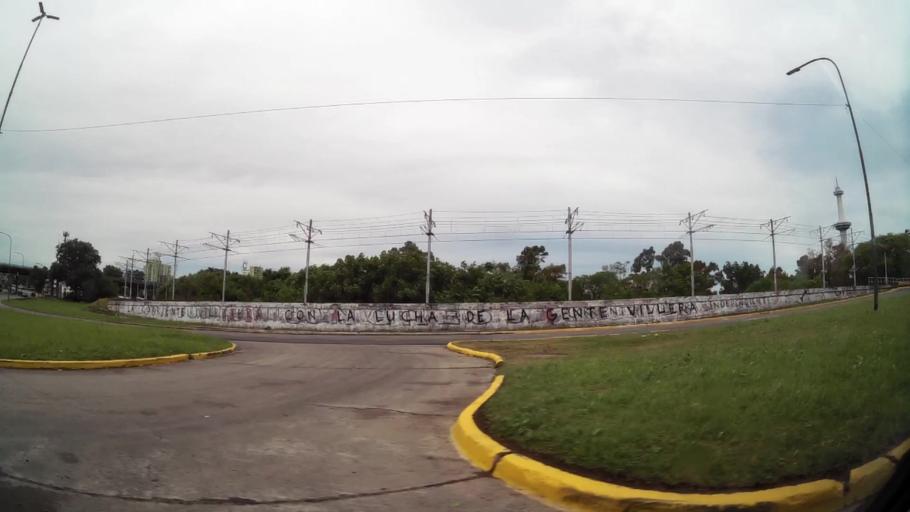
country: AR
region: Buenos Aires F.D.
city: Villa Lugano
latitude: -34.6662
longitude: -58.4521
